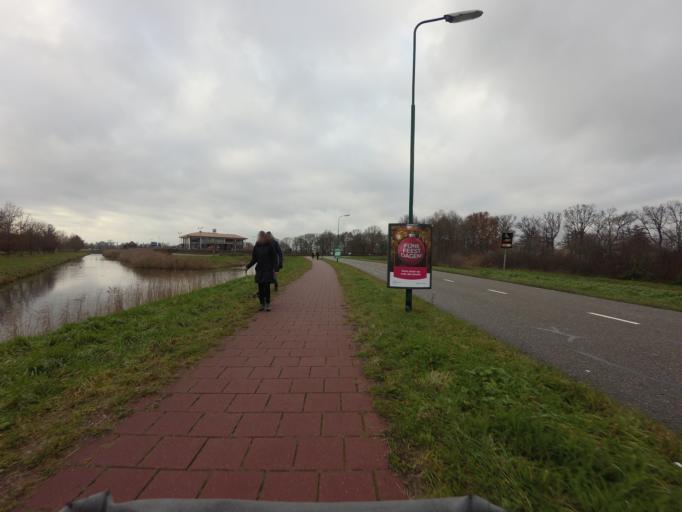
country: NL
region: Utrecht
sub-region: Gemeente Houten
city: Houten
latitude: 52.0362
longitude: 5.1428
